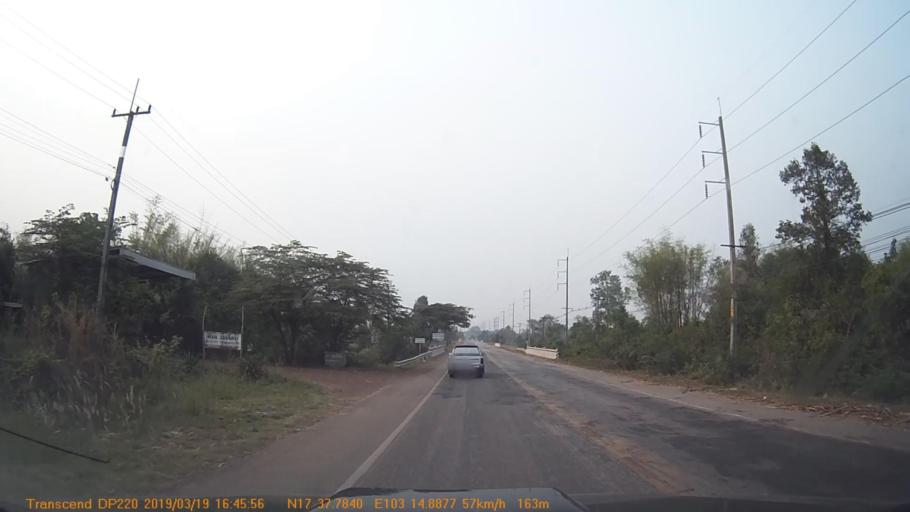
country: TH
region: Changwat Udon Thani
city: Ban Dung
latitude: 17.6301
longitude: 103.2480
